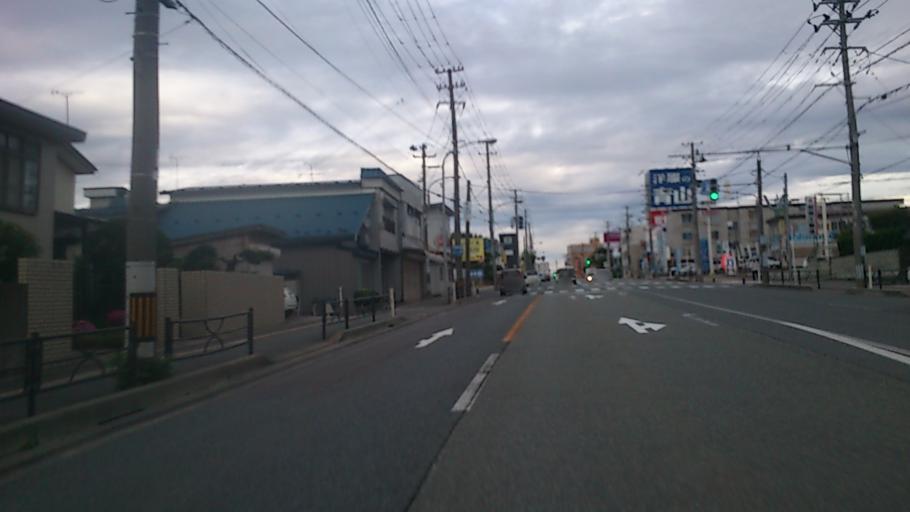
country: JP
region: Akita
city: Akita Shi
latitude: 39.7497
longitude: 140.0696
